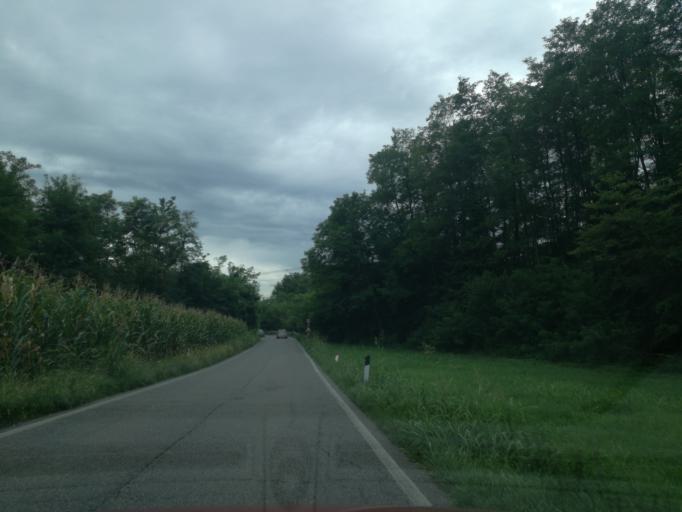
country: IT
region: Lombardy
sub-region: Provincia di Monza e Brianza
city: Mezzago
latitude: 45.6350
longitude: 9.4523
